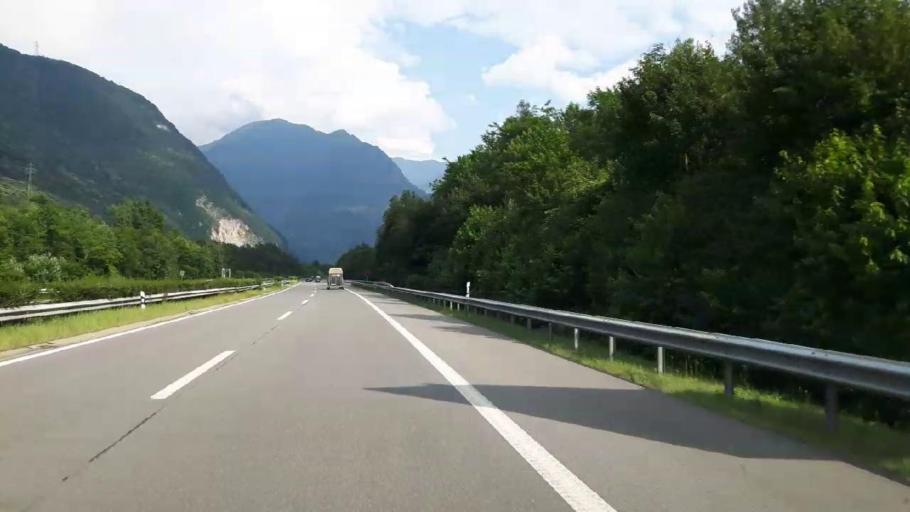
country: CH
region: Ticino
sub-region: Riviera District
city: Claro
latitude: 46.2402
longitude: 9.0208
